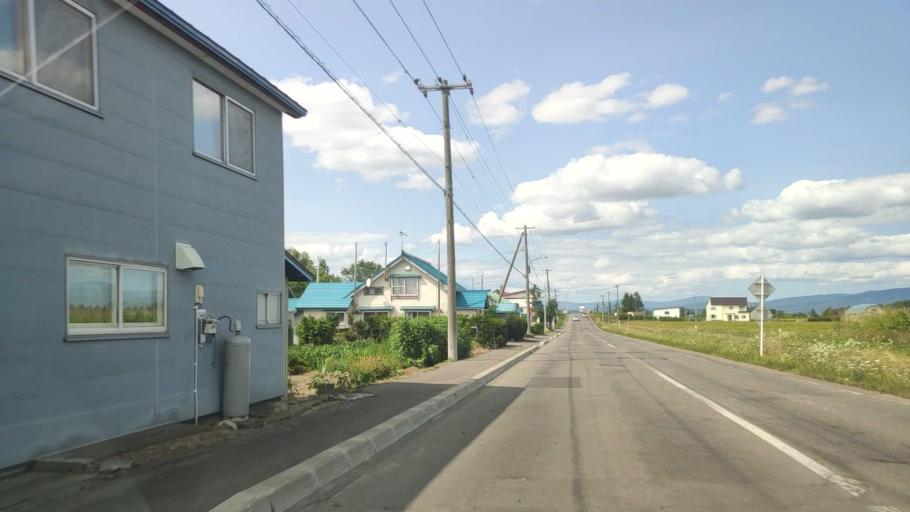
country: JP
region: Hokkaido
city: Nayoro
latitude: 44.2963
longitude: 142.4294
